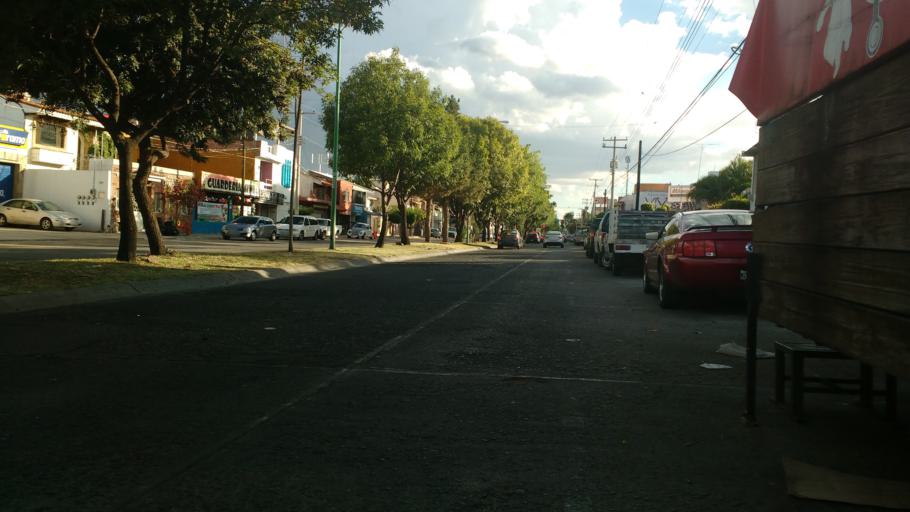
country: MX
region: Guanajuato
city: Leon
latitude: 21.1022
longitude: -101.6462
